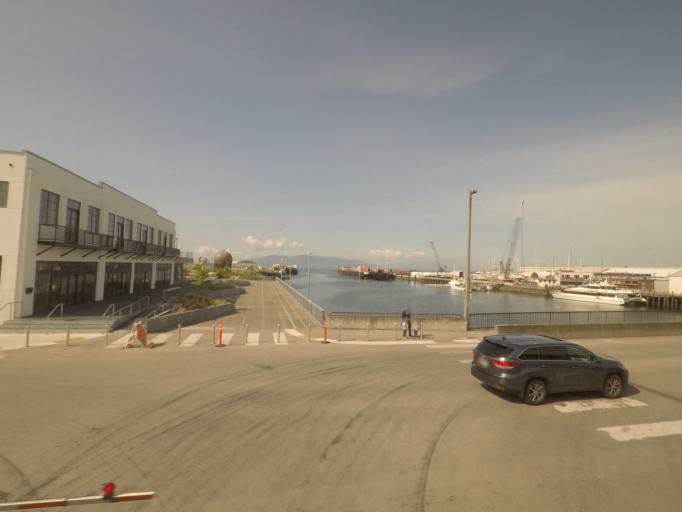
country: US
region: Washington
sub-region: Whatcom County
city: Bellingham
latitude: 48.7520
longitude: -122.4841
